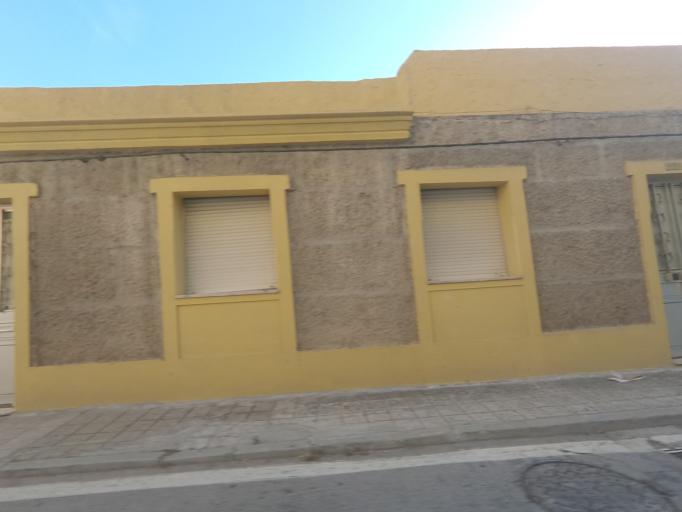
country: PT
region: Vila Real
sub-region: Peso da Regua
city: Godim
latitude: 41.1542
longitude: -7.8343
